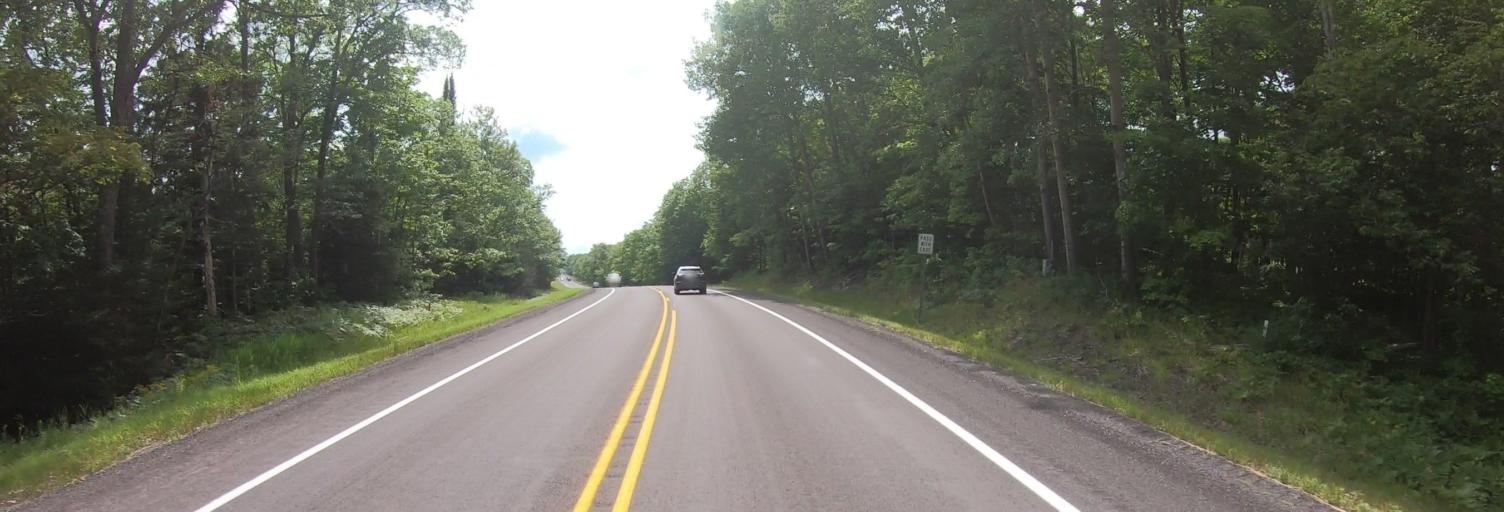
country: US
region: Michigan
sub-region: Houghton County
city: Hancock
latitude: 47.0184
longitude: -88.7412
